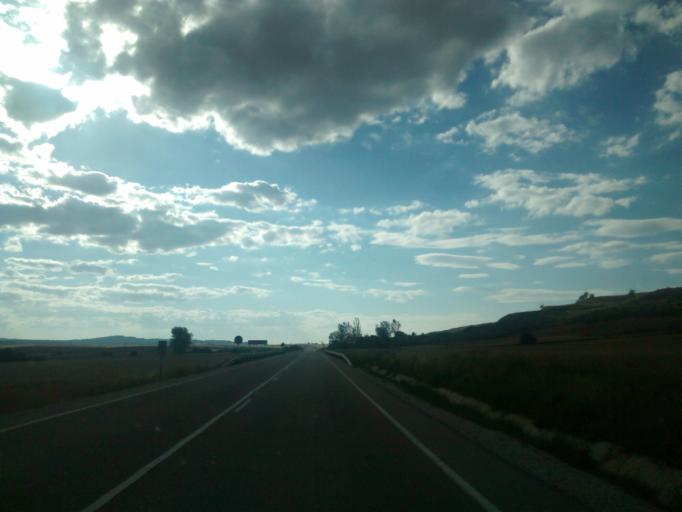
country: ES
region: Castille and Leon
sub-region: Provincia de Burgos
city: Basconcillos del Tozo
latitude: 42.6571
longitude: -3.9043
